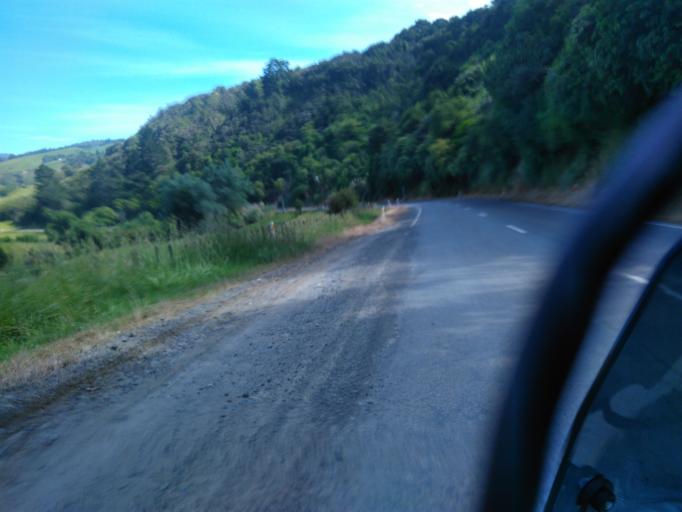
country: NZ
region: Hawke's Bay
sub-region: Wairoa District
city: Wairoa
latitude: -38.8665
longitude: 177.1990
